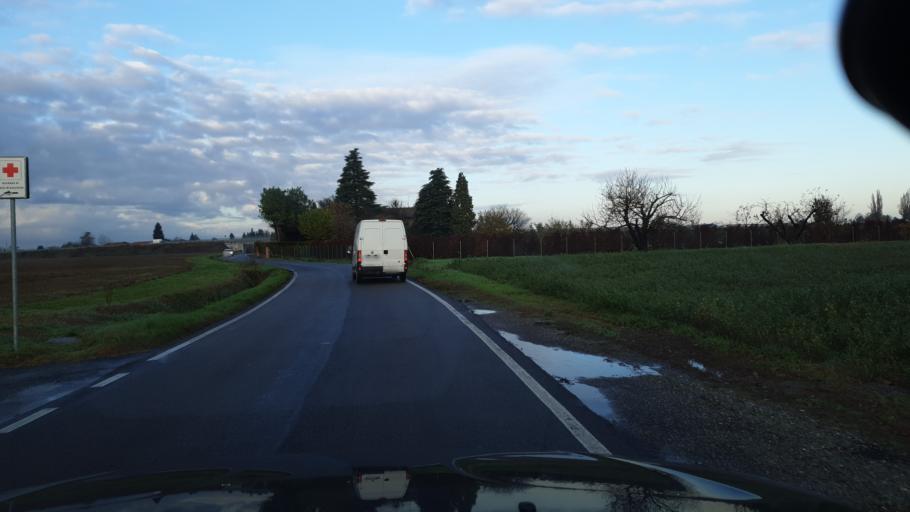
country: IT
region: Emilia-Romagna
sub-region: Provincia di Bologna
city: Crespellano
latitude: 44.5203
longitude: 11.1270
